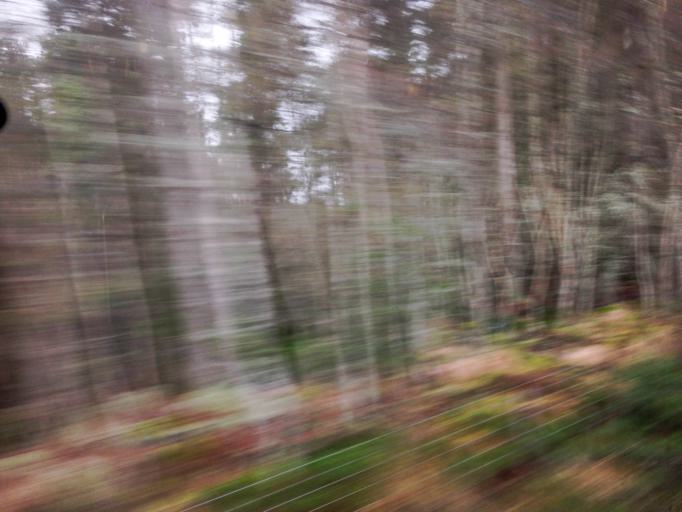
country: GB
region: Scotland
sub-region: Highland
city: Fort William
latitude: 56.8448
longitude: -5.1541
